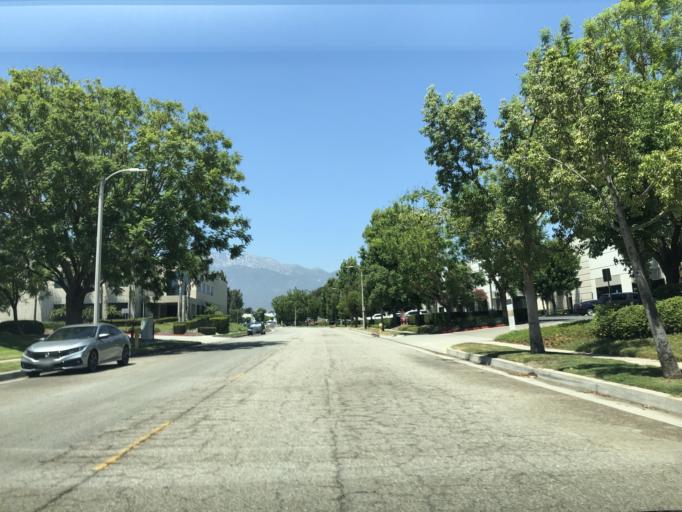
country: US
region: California
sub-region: San Bernardino County
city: Rancho Cucamonga
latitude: 34.0816
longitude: -117.5524
